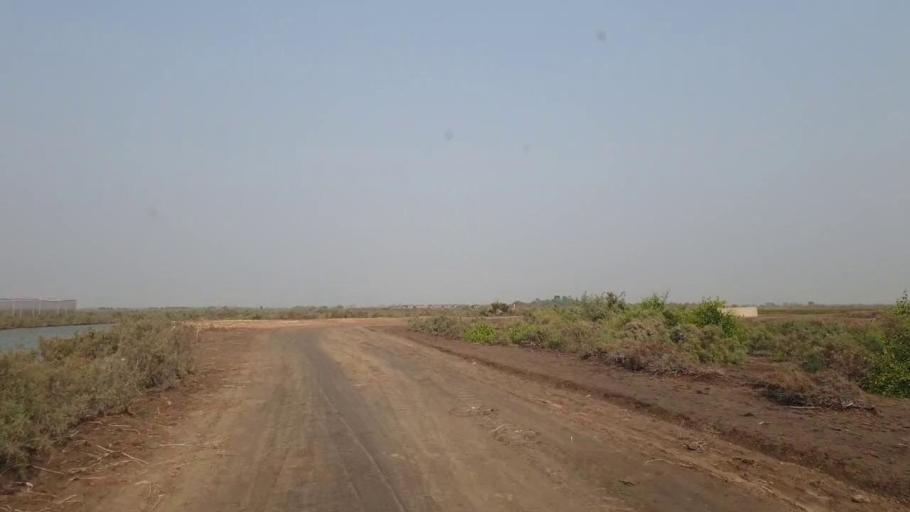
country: PK
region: Sindh
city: Matli
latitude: 25.1010
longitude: 68.6796
